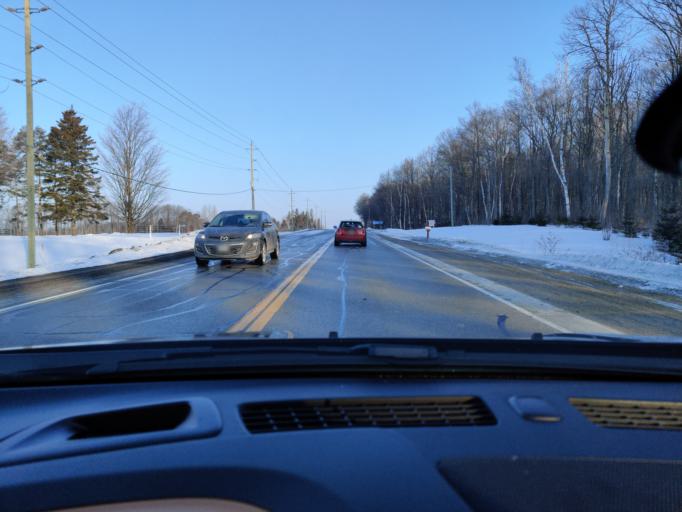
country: CA
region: Ontario
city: Angus
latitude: 44.3928
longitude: -79.7974
